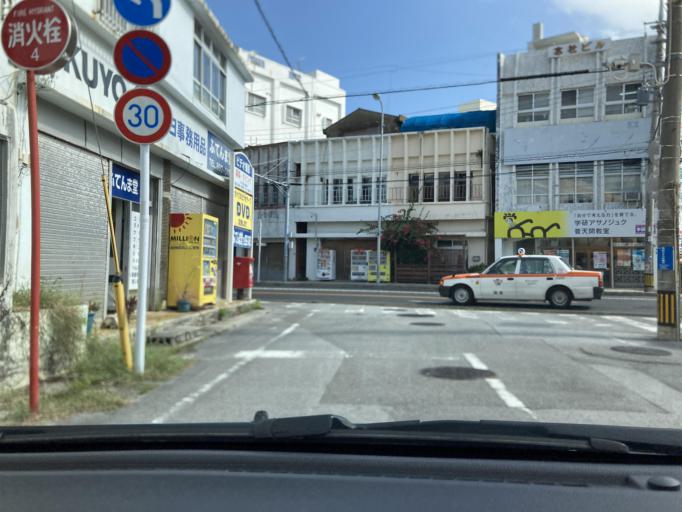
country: JP
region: Okinawa
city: Chatan
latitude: 26.2915
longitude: 127.7772
